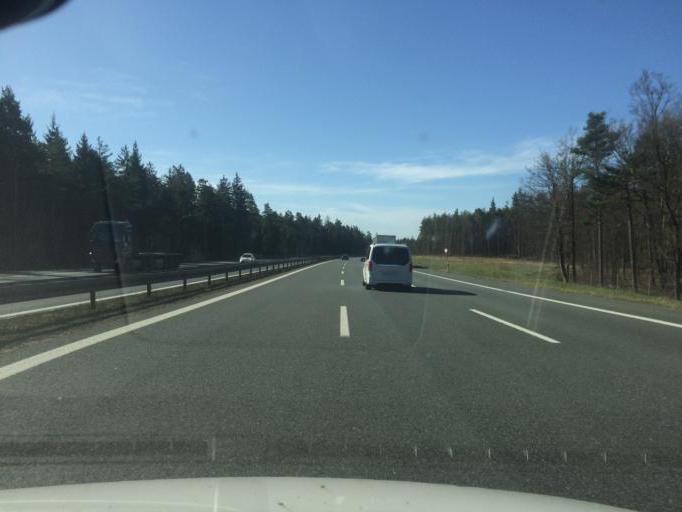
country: DE
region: Bavaria
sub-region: Upper Franconia
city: Gesees
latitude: 49.8591
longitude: 11.5181
